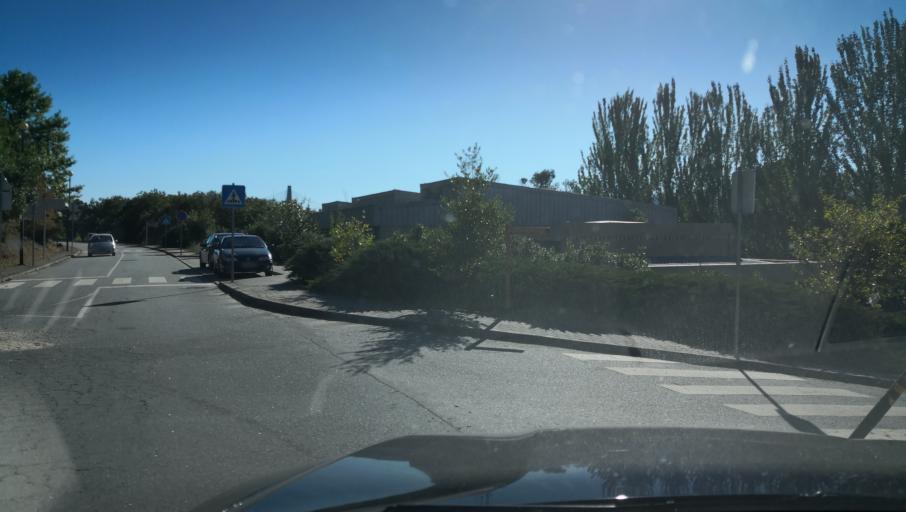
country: PT
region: Vila Real
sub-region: Vila Real
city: Vila Real
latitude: 41.2850
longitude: -7.7438
